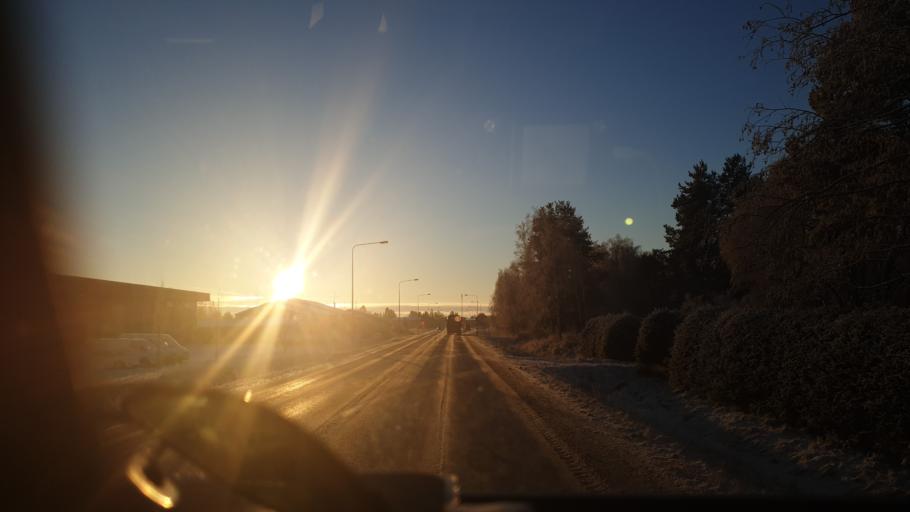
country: FI
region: Northern Ostrobothnia
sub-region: Ylivieska
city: Kalajoki
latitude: 64.2684
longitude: 23.9491
